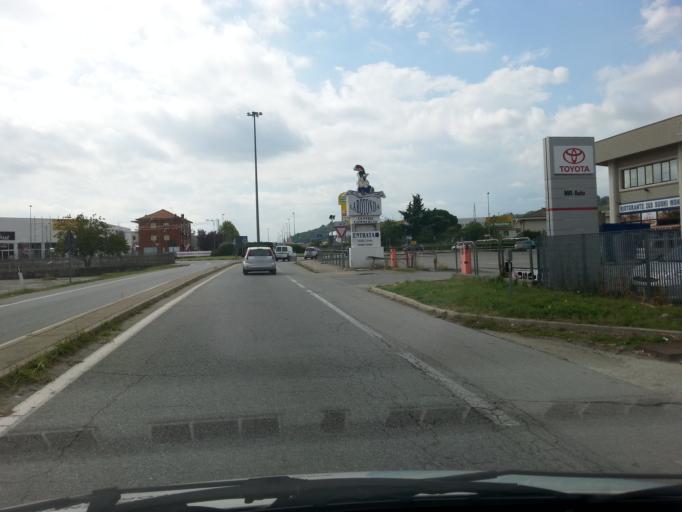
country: IT
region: Piedmont
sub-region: Provincia di Torino
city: Frossasco
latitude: 44.9125
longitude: 7.3626
